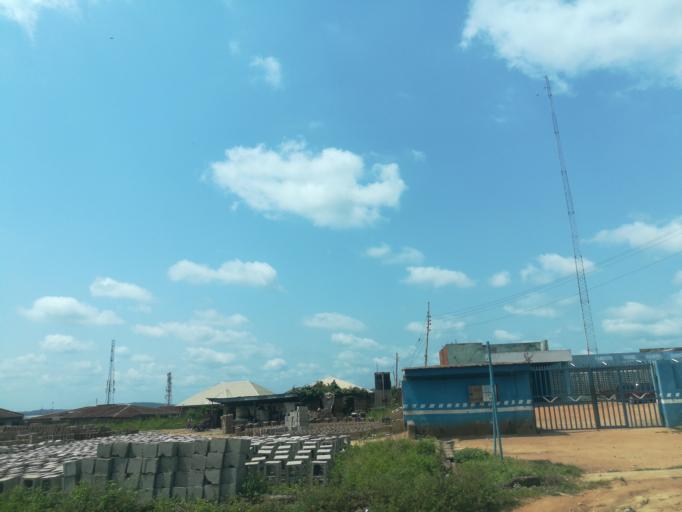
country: NG
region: Oyo
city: Moniya
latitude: 7.5394
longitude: 3.9114
